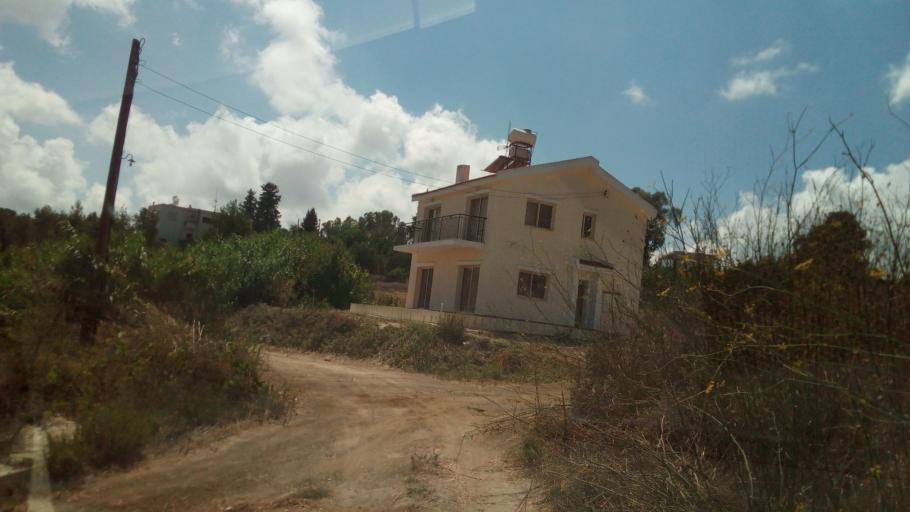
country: CY
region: Pafos
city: Tala
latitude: 34.8840
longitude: 32.4845
